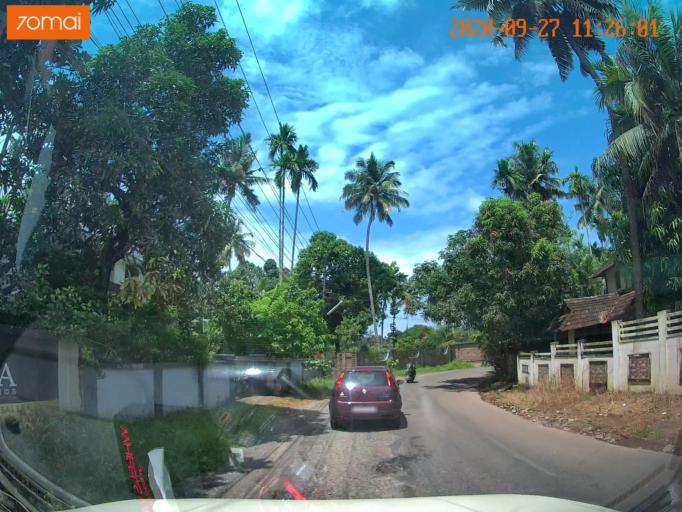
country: IN
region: Kerala
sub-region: Thrissur District
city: Thanniyam
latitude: 10.4145
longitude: 76.1543
